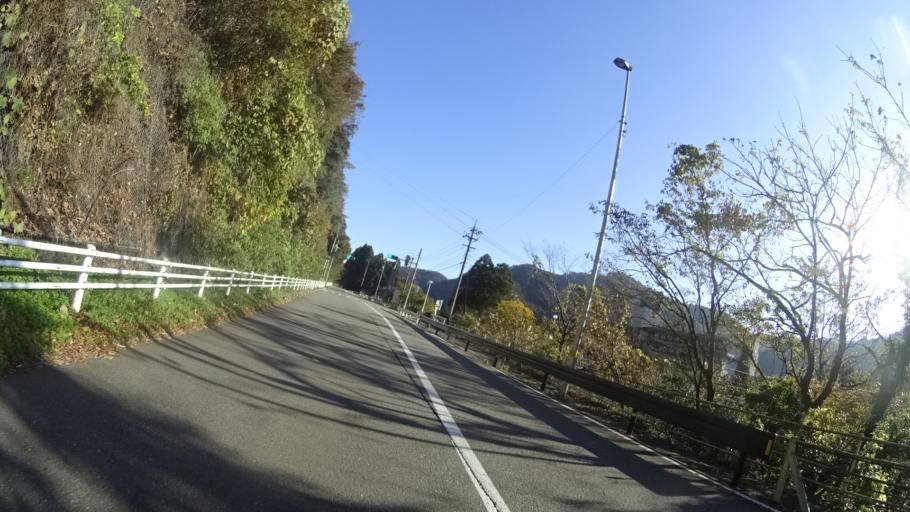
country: JP
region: Fukui
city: Maruoka
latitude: 36.2322
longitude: 136.3618
